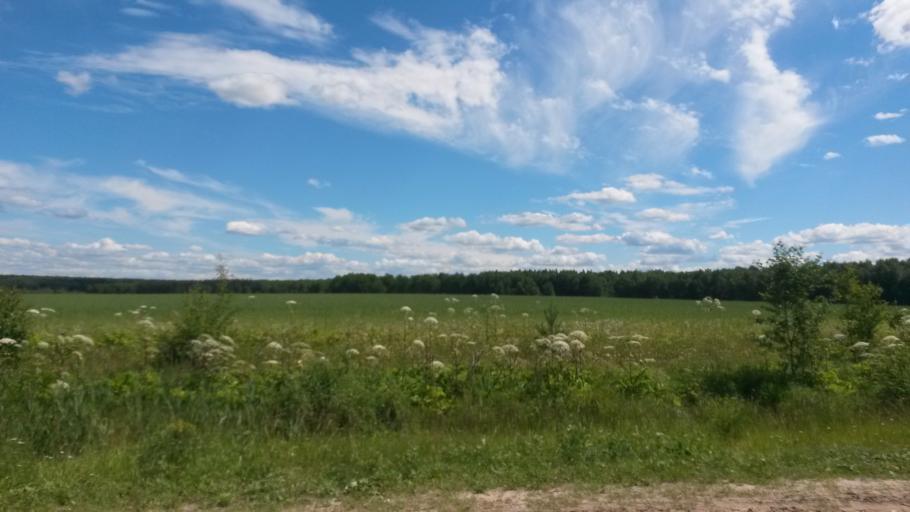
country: RU
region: Ivanovo
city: Rodniki
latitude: 57.1202
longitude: 41.7908
